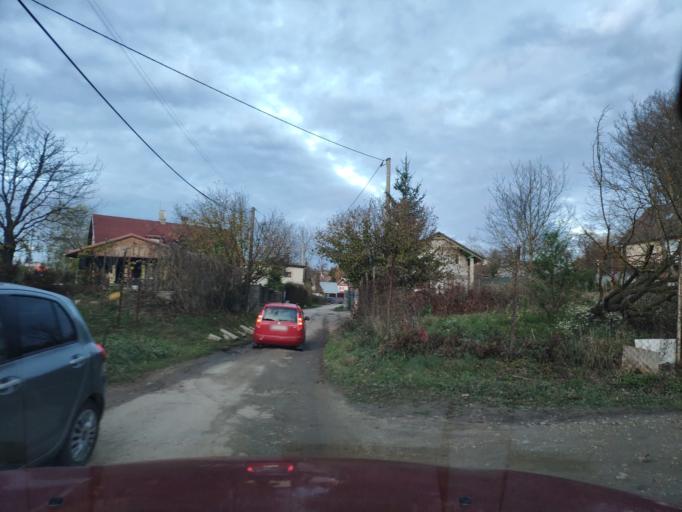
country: SK
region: Kosicky
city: Kosice
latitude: 48.6686
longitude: 21.3554
